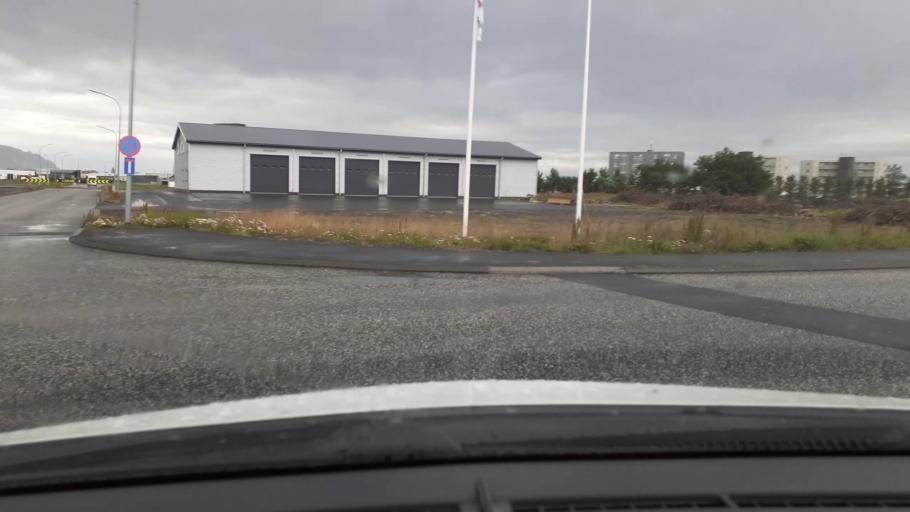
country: IS
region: West
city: Akranes
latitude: 64.3259
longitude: -22.0596
